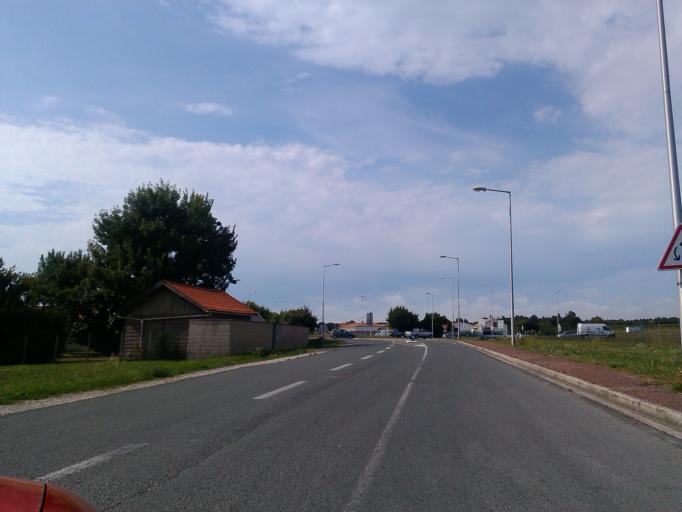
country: FR
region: Poitou-Charentes
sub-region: Departement de la Charente-Maritime
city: Arvert
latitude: 45.7590
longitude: -1.1241
